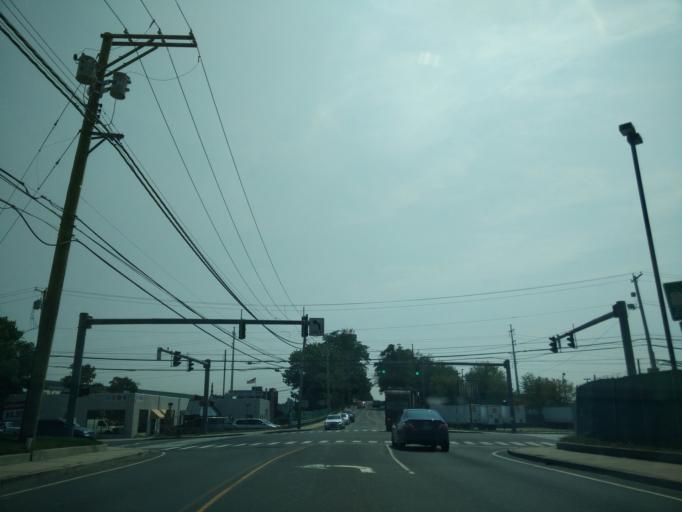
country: US
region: Connecticut
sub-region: Fairfield County
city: Bridgeport
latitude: 41.1639
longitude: -73.2335
